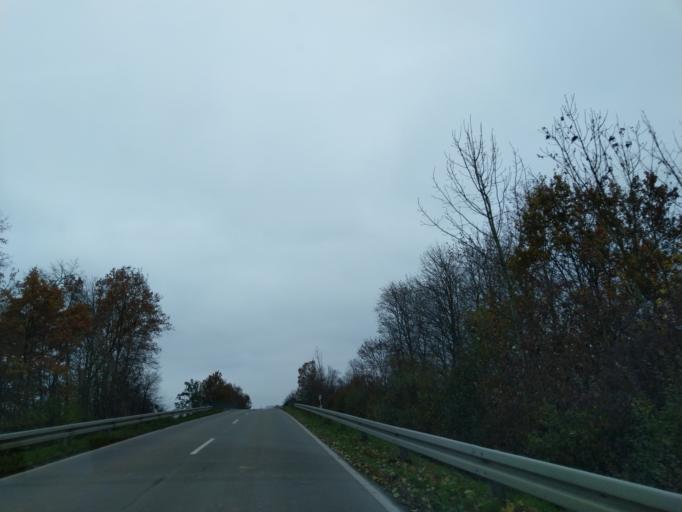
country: DE
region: Bavaria
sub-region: Lower Bavaria
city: Otzing
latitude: 48.7675
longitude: 12.7800
